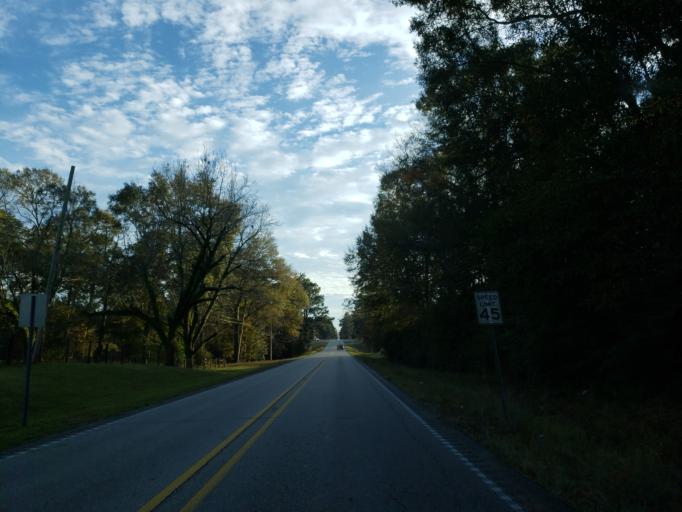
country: US
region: Mississippi
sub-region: Lamar County
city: Purvis
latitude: 31.1278
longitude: -89.4071
